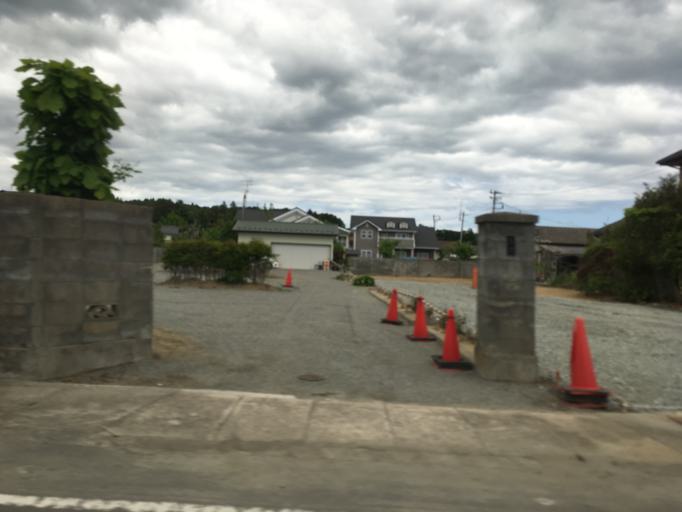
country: JP
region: Fukushima
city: Namie
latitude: 37.4938
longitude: 141.0138
